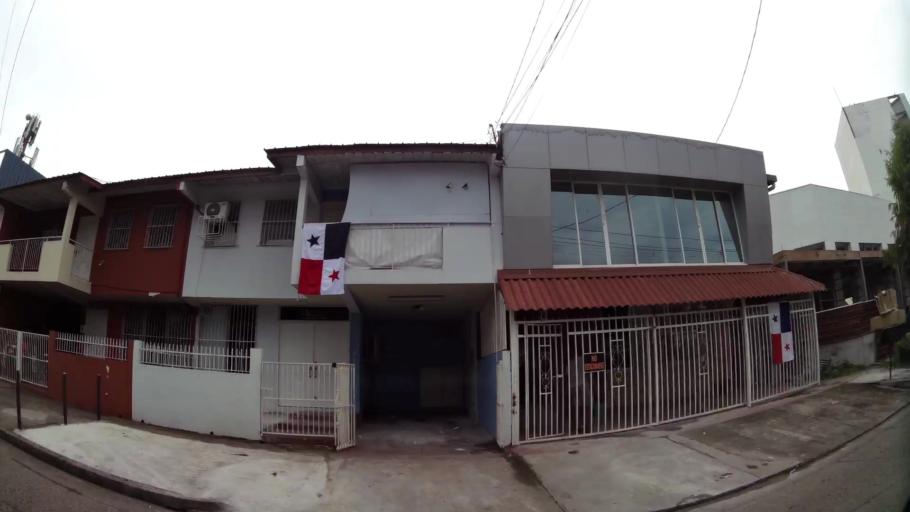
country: PA
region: Panama
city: Panama
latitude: 9.0196
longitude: -79.5266
